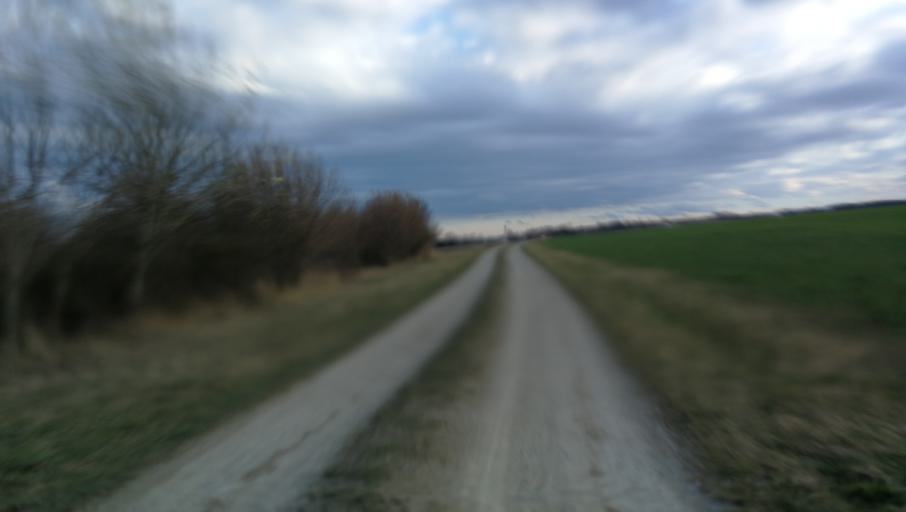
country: DE
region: Bavaria
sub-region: Upper Bavaria
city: Fuerstenfeldbruck
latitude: 48.2057
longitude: 11.2156
